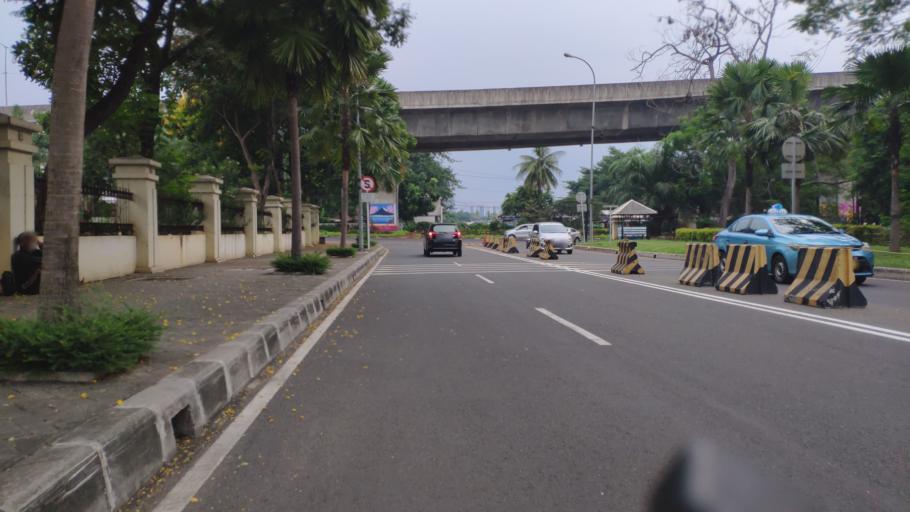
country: ID
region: Jakarta Raya
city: Jakarta
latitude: -6.2249
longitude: 106.8356
